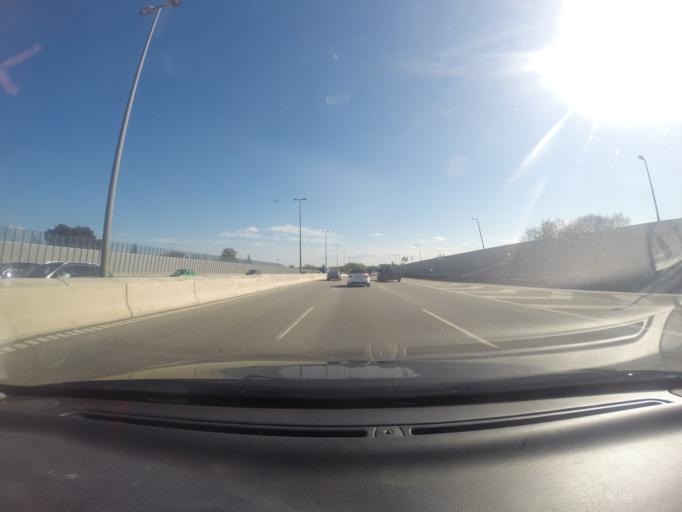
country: DK
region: Capital Region
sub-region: Herlev Kommune
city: Herlev
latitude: 55.7190
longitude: 12.4549
